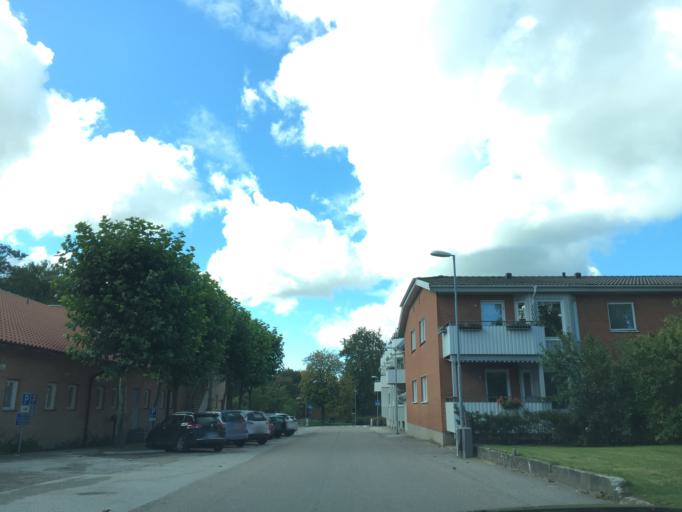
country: SE
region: Skane
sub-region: Sjobo Kommun
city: Sjoebo
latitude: 55.6331
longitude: 13.7050
